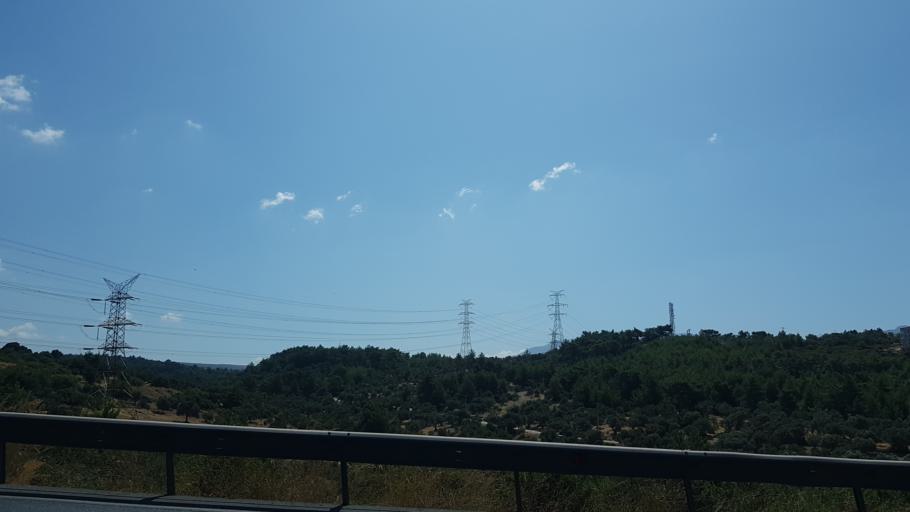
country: TR
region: Izmir
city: Bornova
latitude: 38.4794
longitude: 27.2375
